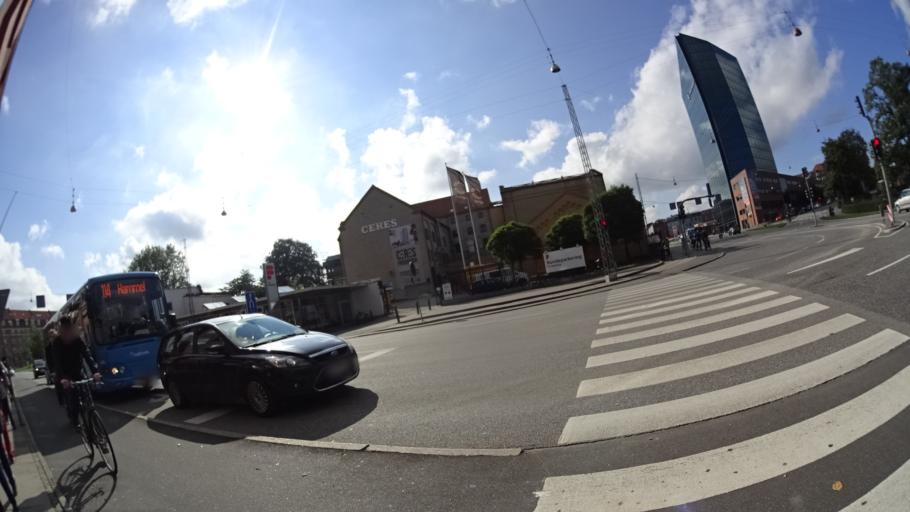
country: DK
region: Central Jutland
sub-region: Arhus Kommune
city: Arhus
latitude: 56.1575
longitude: 10.1951
